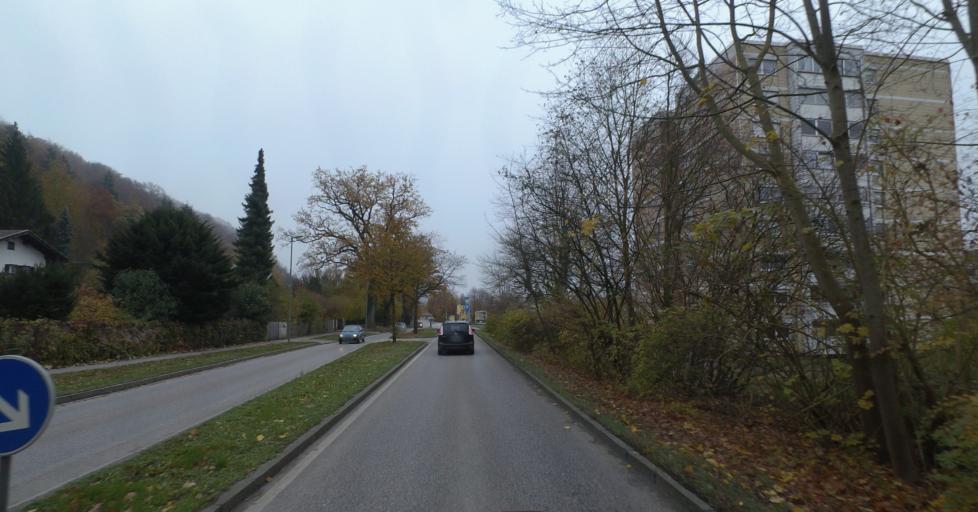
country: DE
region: Bavaria
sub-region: Upper Bavaria
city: Trostberg an der Alz
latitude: 48.0256
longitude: 12.5393
